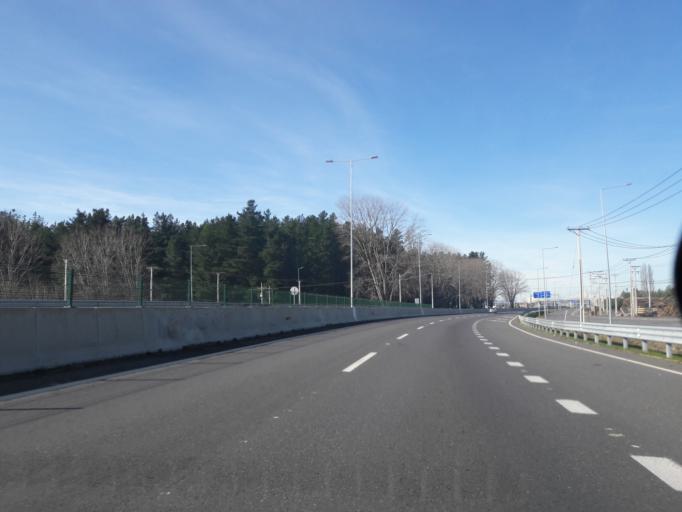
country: CL
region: Biobio
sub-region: Provincia de Biobio
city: Cabrero
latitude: -37.0321
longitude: -72.4223
